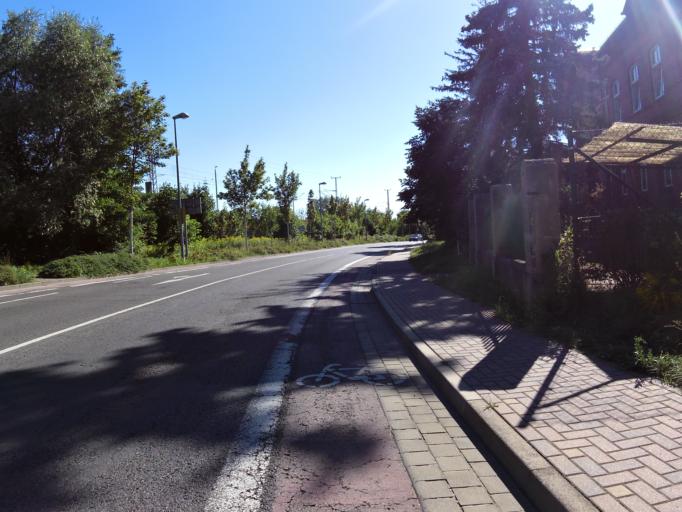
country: DE
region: Saxony-Anhalt
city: Wittenburg
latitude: 51.8649
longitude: 12.6577
